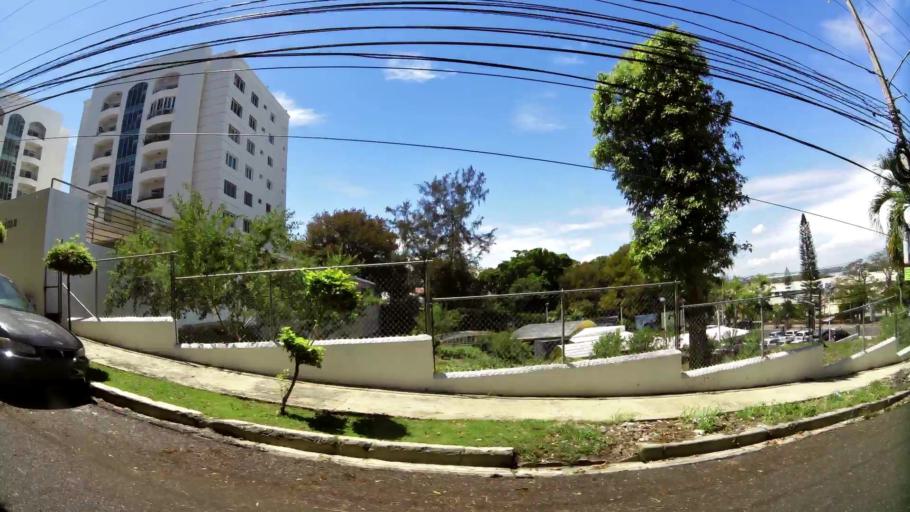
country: DO
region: Santiago
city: Santiago de los Caballeros
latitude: 19.4567
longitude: -70.6918
